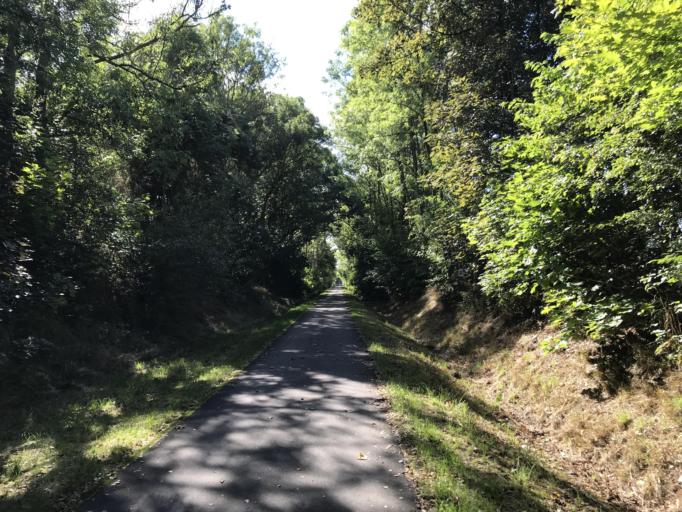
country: DE
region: Hesse
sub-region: Regierungsbezirk Kassel
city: Sachsenhausen
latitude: 51.2706
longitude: 8.9928
